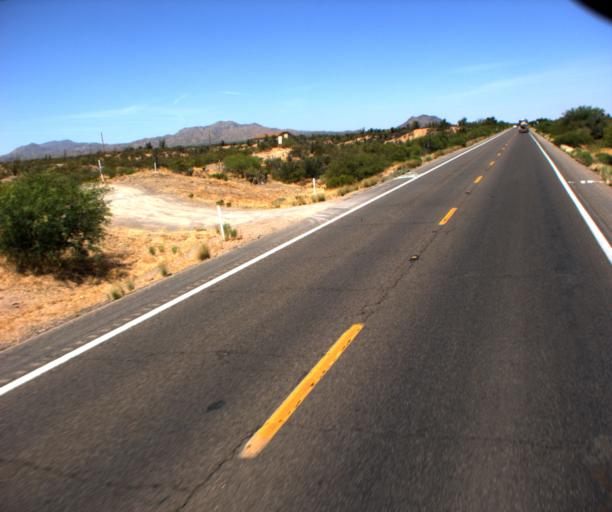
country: US
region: Arizona
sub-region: Gila County
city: Peridot
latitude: 33.3071
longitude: -110.4918
